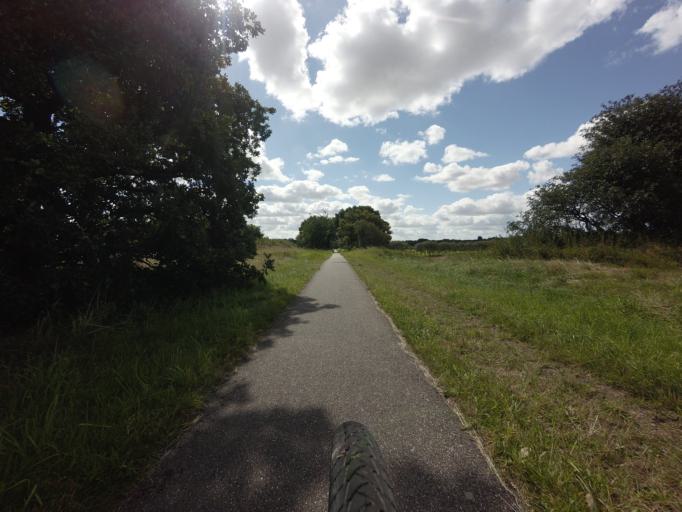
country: DK
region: Central Jutland
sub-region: Horsens Kommune
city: Horsens
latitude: 55.9170
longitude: 9.7684
